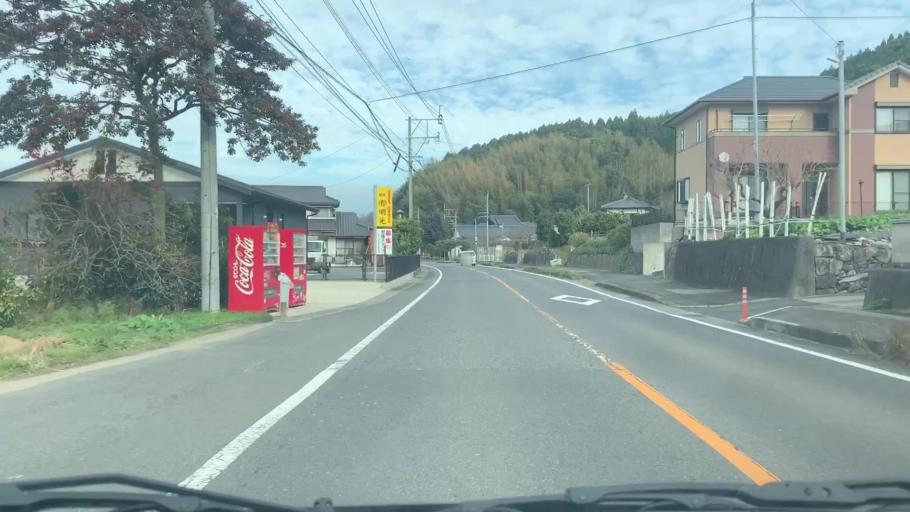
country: JP
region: Saga Prefecture
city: Karatsu
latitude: 33.3888
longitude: 129.9877
